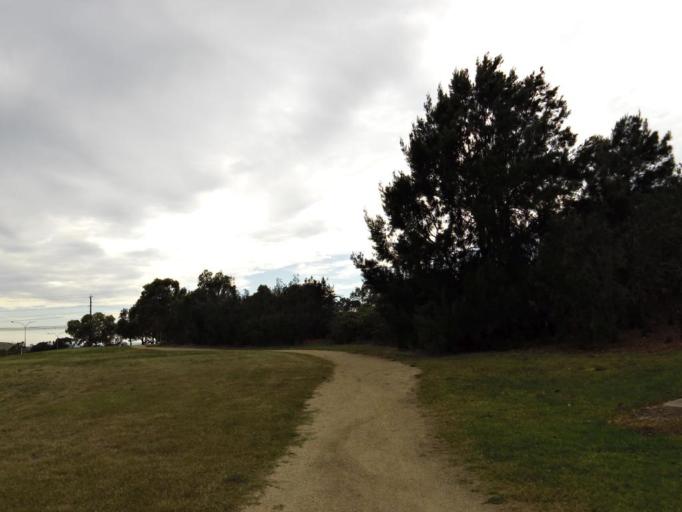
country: AU
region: Victoria
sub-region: Whittlesea
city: Mill Park
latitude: -37.6438
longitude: 145.0664
